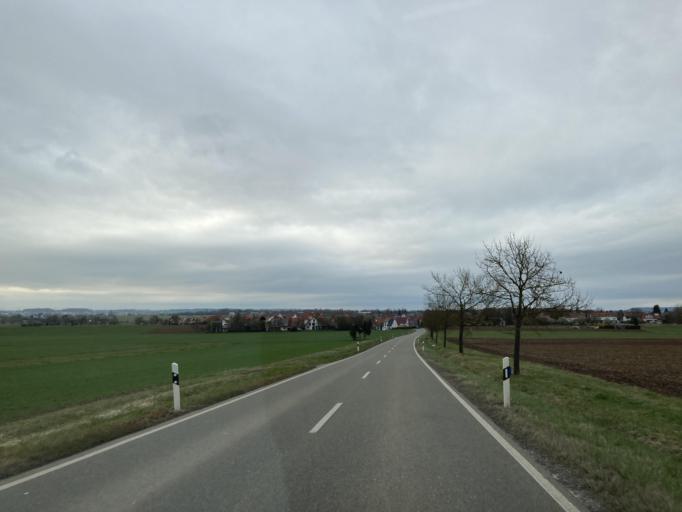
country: DE
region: Baden-Wuerttemberg
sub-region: Regierungsbezirk Stuttgart
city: Bondorf
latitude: 48.5207
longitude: 8.8687
